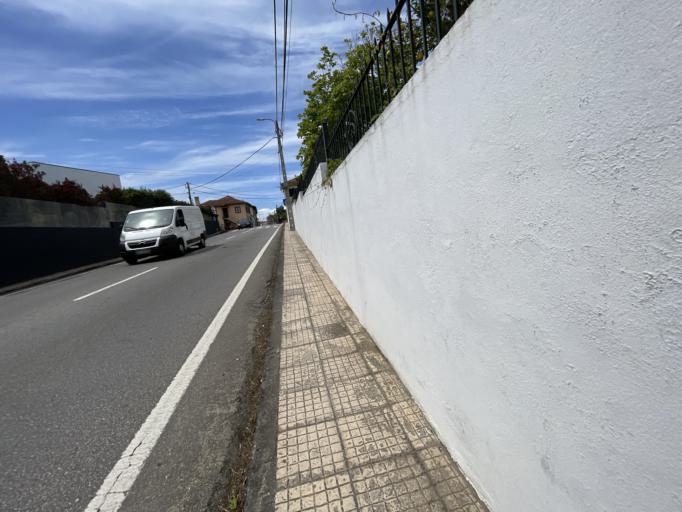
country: PT
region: Aveiro
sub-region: Ovar
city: Cortegaca
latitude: 40.9413
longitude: -8.6189
